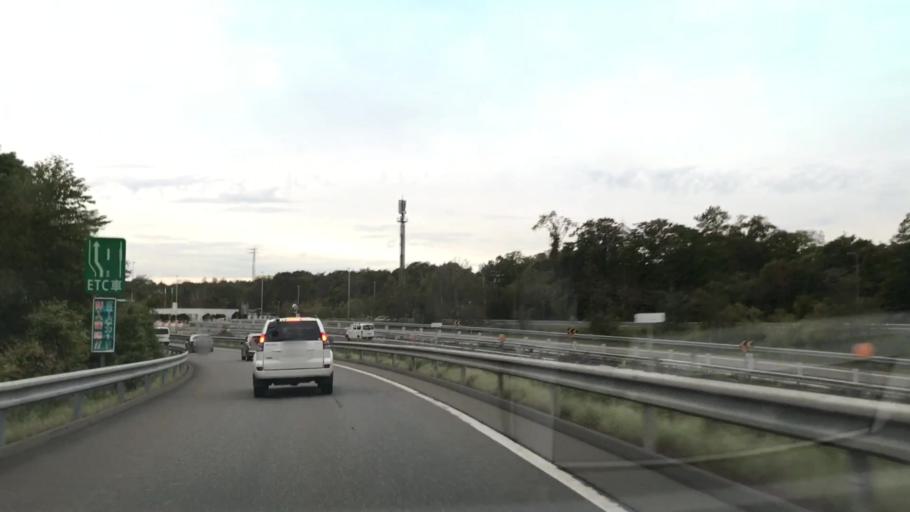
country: JP
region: Hokkaido
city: Tomakomai
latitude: 42.7086
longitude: 141.6580
